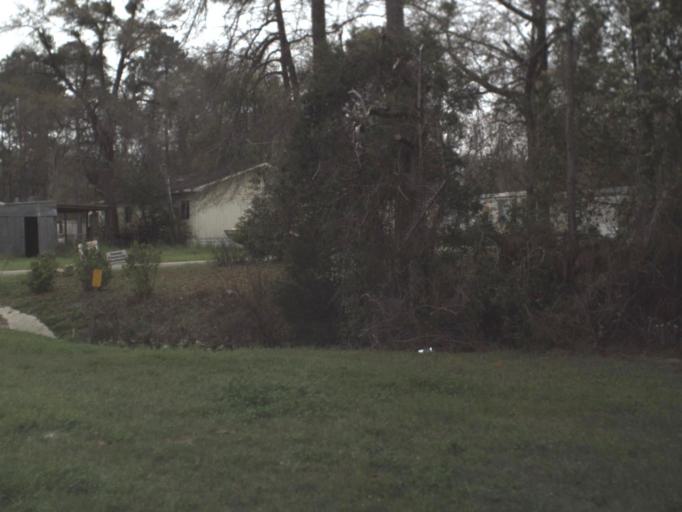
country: US
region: Florida
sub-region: Gulf County
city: Wewahitchka
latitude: 30.0169
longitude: -84.9793
